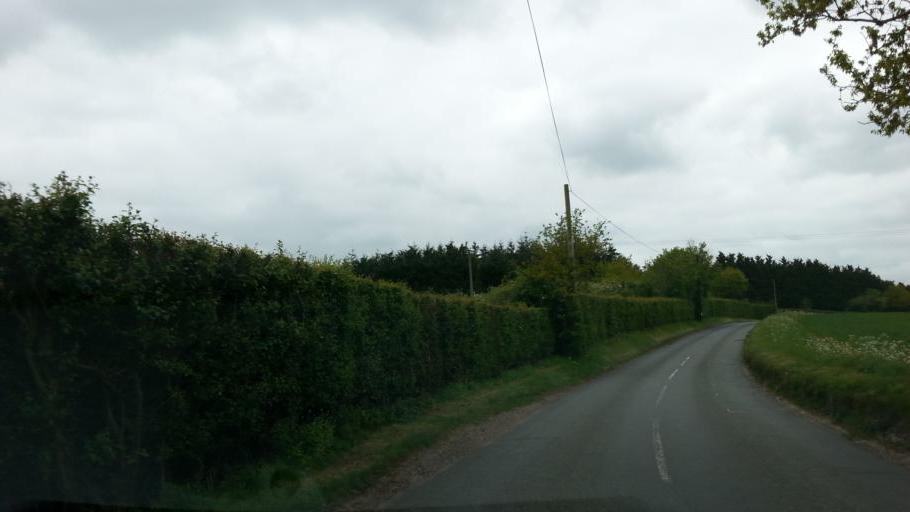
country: GB
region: England
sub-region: Suffolk
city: Hadleigh
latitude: 52.0719
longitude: 0.9257
